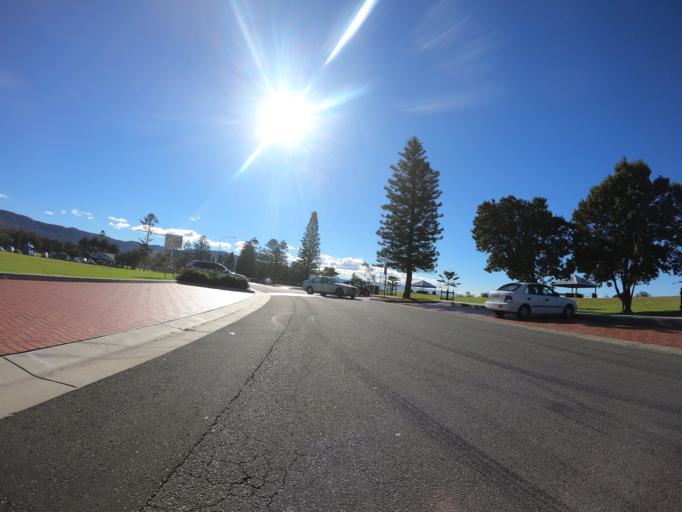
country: AU
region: New South Wales
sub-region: Wollongong
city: Wollongong
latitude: -34.4117
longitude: 150.9014
